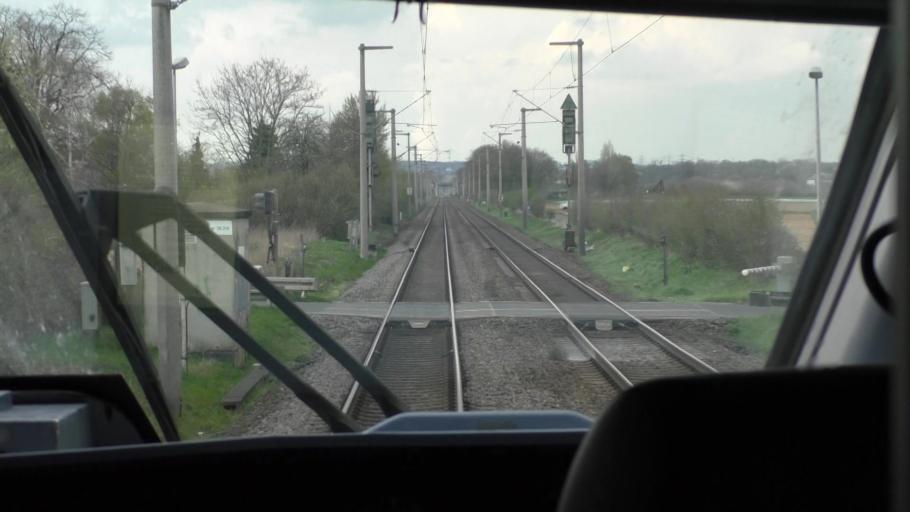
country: DE
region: North Rhine-Westphalia
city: Wesseling
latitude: 50.8035
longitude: 6.9462
